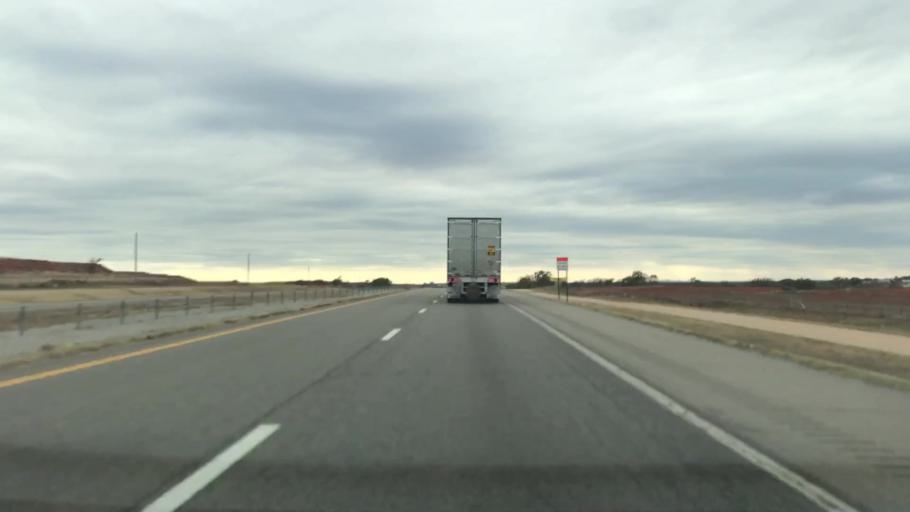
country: US
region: Oklahoma
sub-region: Washita County
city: Burns Flat
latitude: 35.4622
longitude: -99.1467
